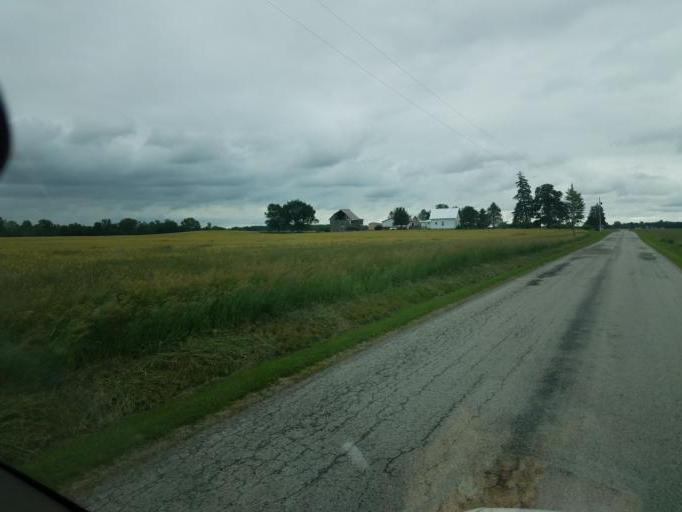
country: US
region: Ohio
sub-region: Morrow County
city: Cardington
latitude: 40.5647
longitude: -82.9193
